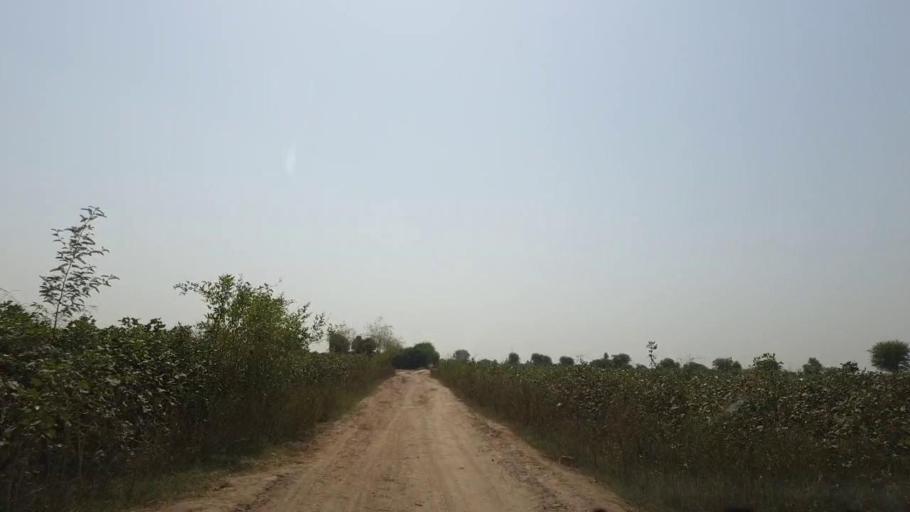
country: PK
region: Sindh
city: Jhol
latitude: 25.8507
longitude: 69.0296
